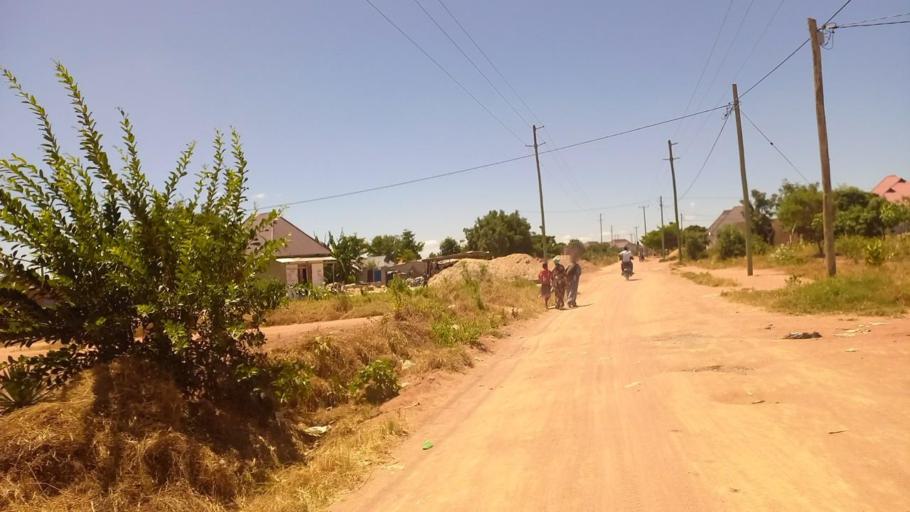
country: TZ
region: Dodoma
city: Dodoma
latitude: -6.1306
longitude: 35.7260
